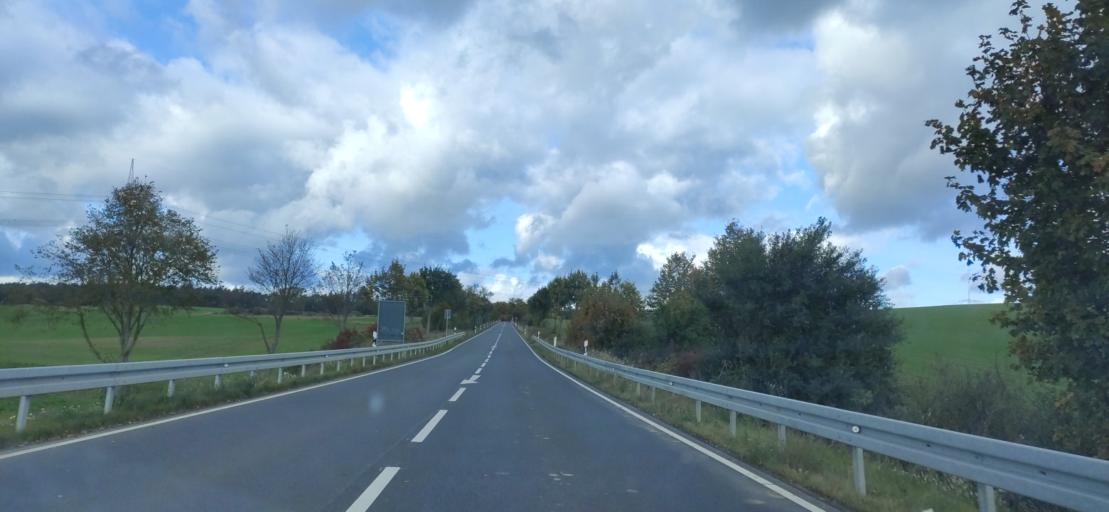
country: DE
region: Mecklenburg-Vorpommern
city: Grabowhofe
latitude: 53.5886
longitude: 12.6239
